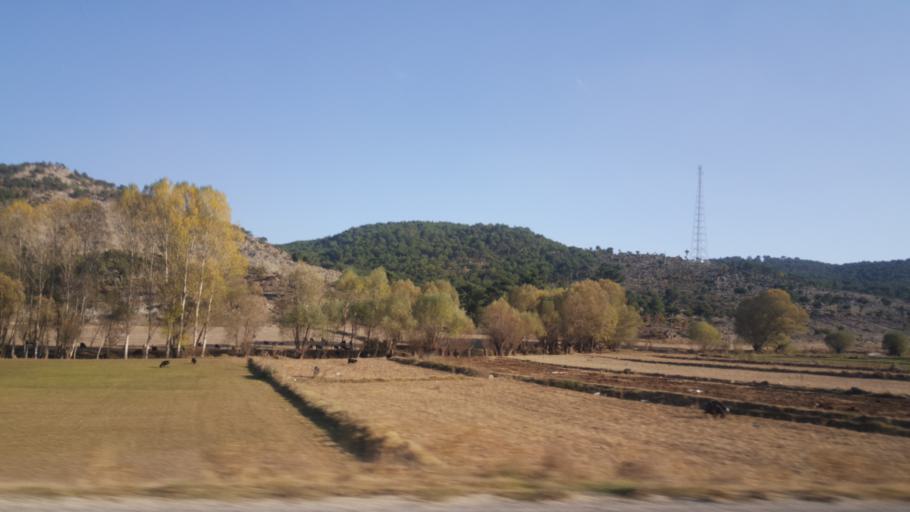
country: TR
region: Eskisehir
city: Kirka
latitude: 39.1281
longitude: 30.5921
